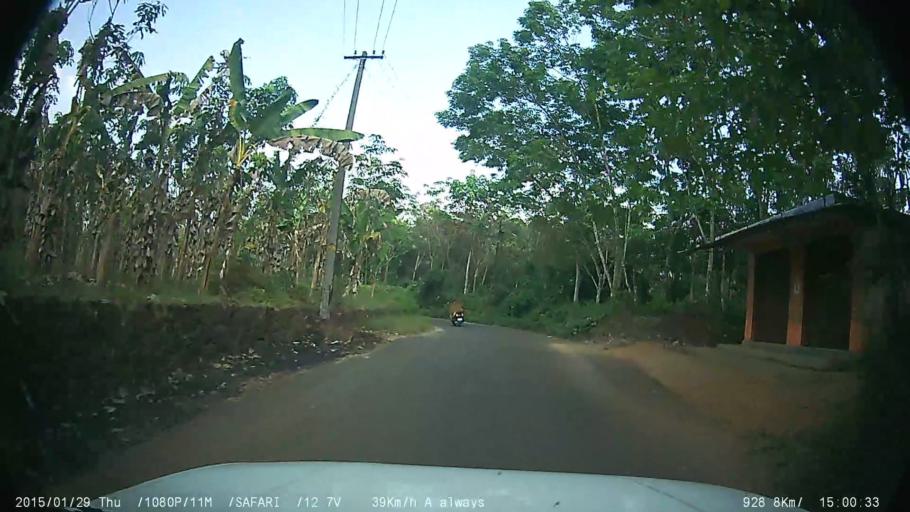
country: IN
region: Kerala
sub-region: Kottayam
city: Palackattumala
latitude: 9.7274
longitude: 76.5675
